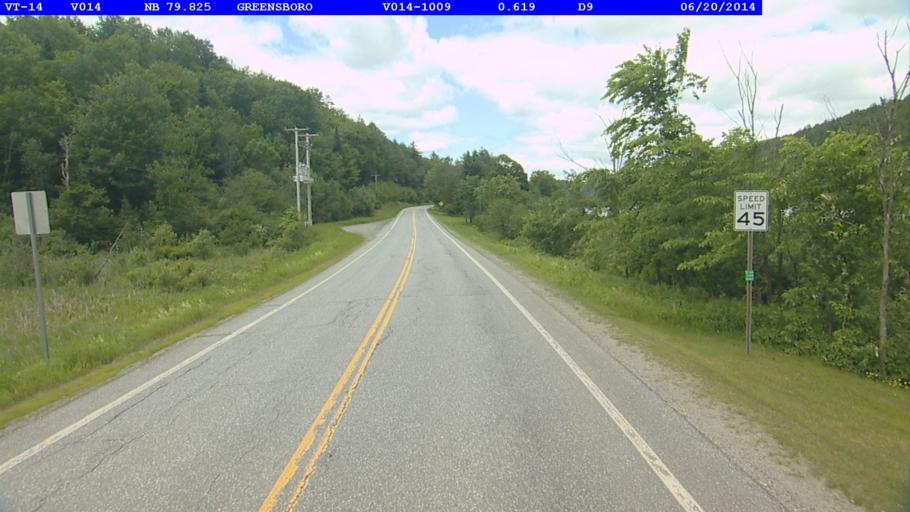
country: US
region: Vermont
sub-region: Caledonia County
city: Hardwick
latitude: 44.5880
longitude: -72.3590
